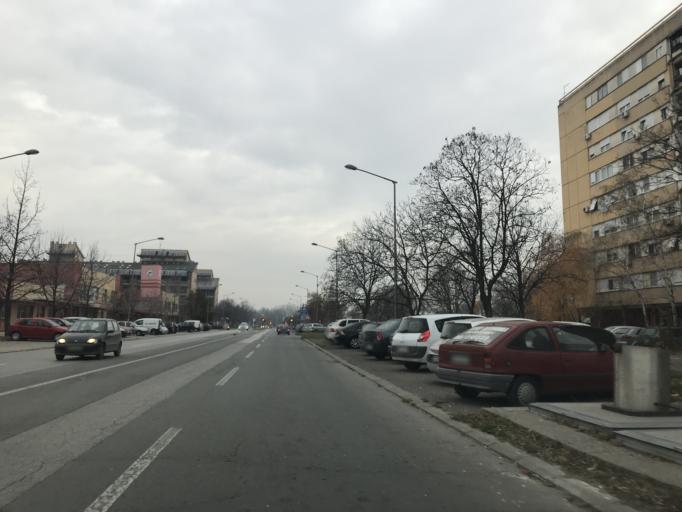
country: RS
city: Veternik
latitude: 45.2524
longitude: 19.7964
